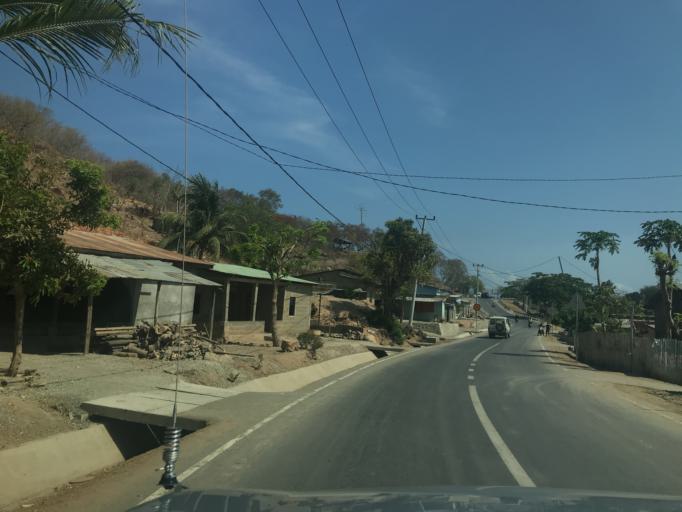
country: TL
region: Dili
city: Dili
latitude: -8.5609
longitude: 125.5227
